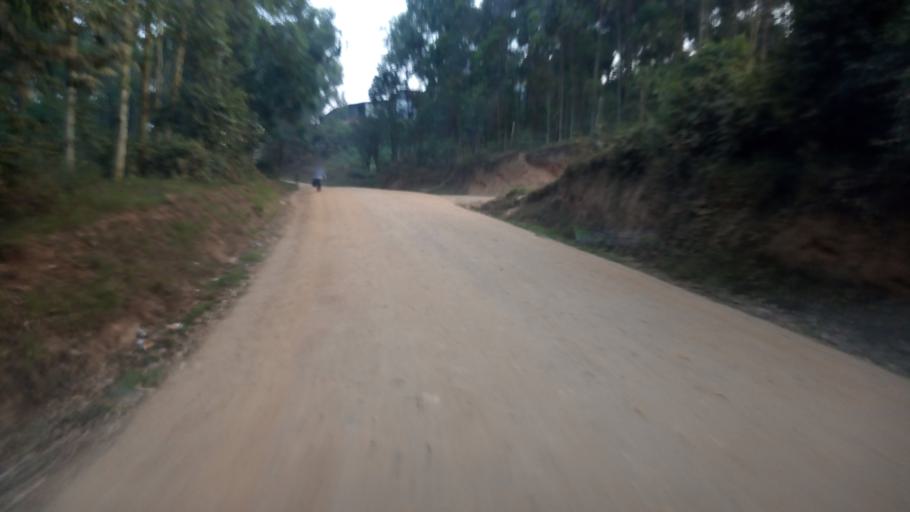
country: UG
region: Western Region
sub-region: Rukungiri District
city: Rukungiri
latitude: -0.7757
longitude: 29.9246
